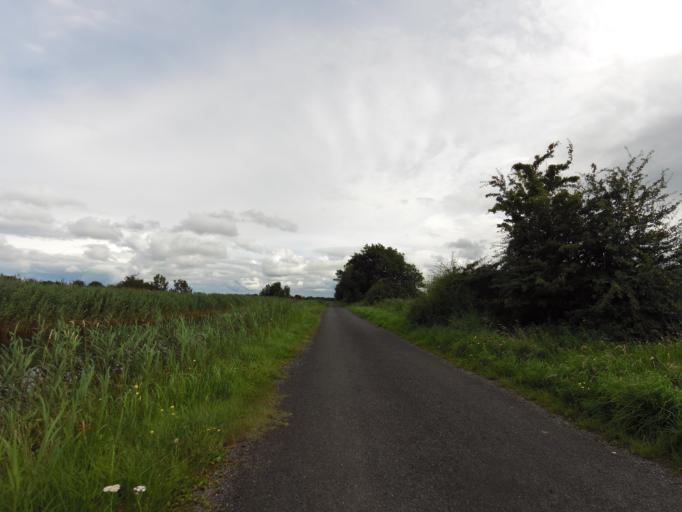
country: IE
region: Leinster
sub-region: An Longfort
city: Edgeworthstown
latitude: 53.5786
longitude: -7.5322
